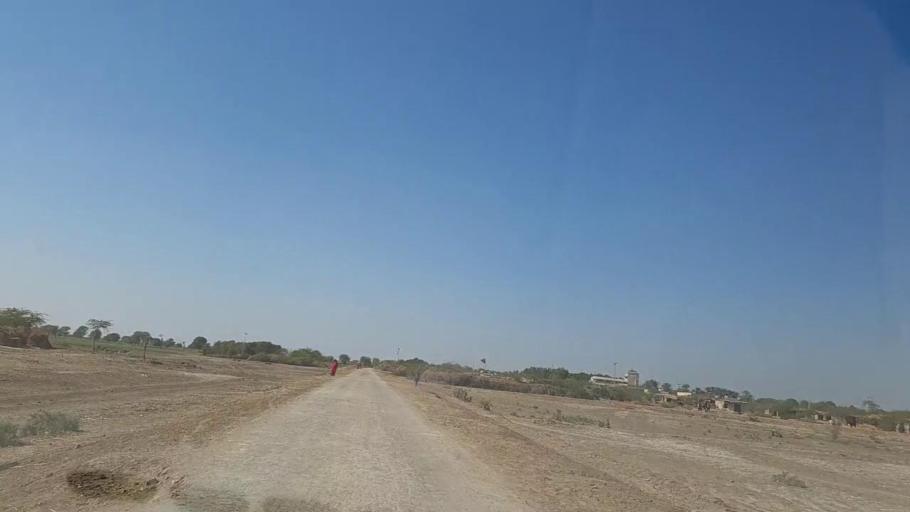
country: PK
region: Sindh
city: Digri
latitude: 25.1230
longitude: 69.0755
